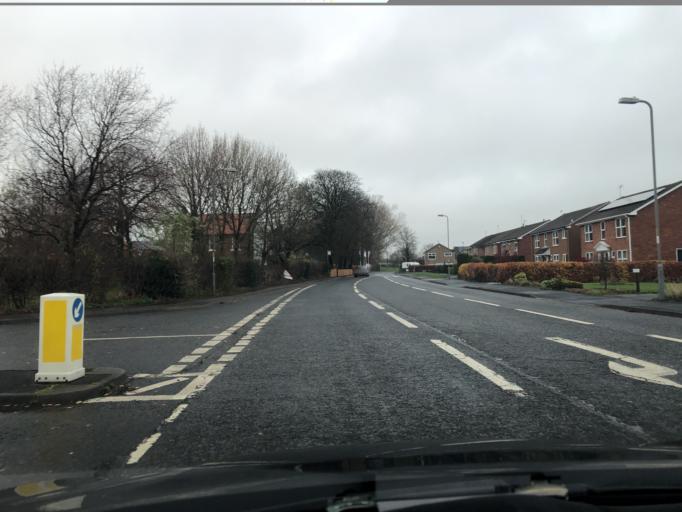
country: GB
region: England
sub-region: North Yorkshire
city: Stokesley
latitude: 54.4772
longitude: -1.1876
